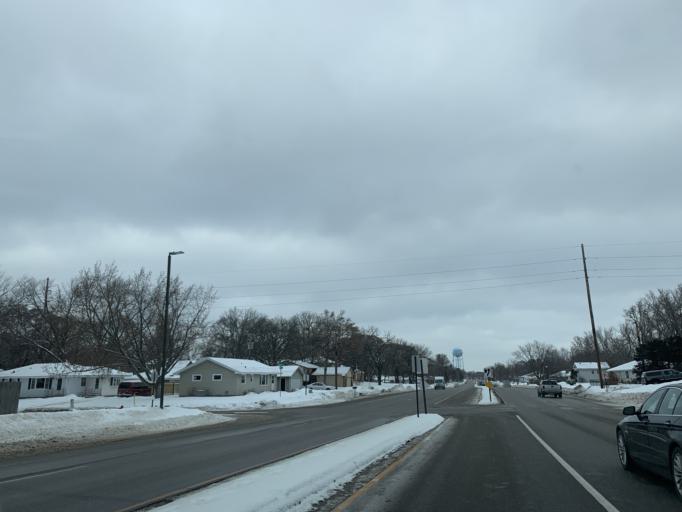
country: US
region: Minnesota
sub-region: Anoka County
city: Blaine
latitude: 45.1672
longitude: -93.2765
